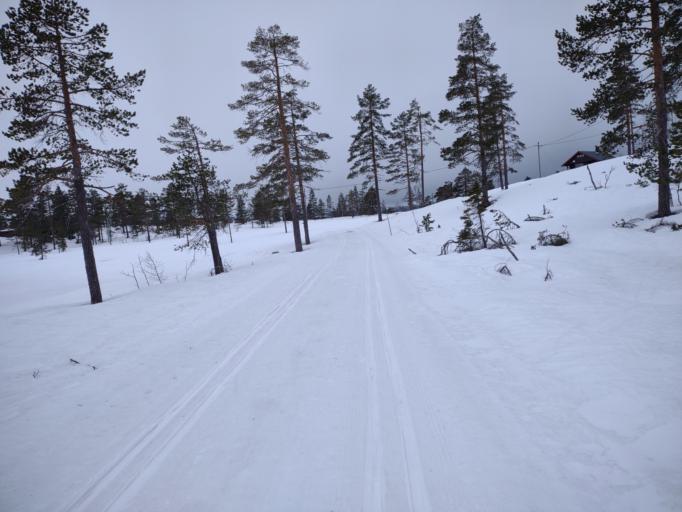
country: NO
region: Buskerud
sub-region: Flesberg
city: Lampeland
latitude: 59.7957
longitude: 9.4361
